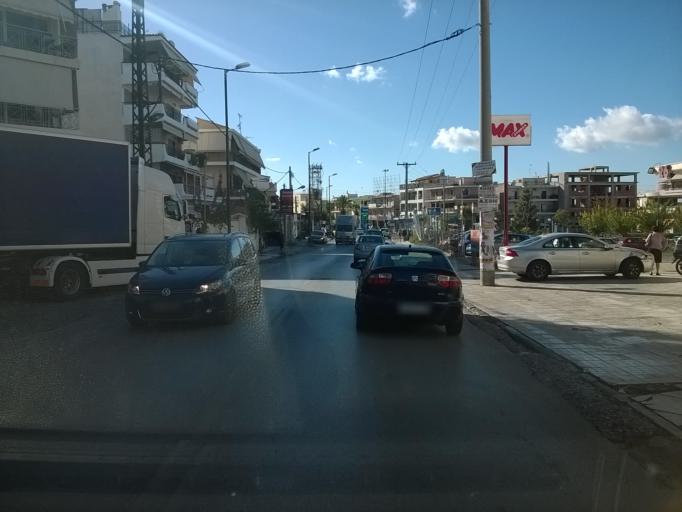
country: GR
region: Attica
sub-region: Nomarchia Athinas
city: Argyroupoli
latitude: 37.8935
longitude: 23.7609
